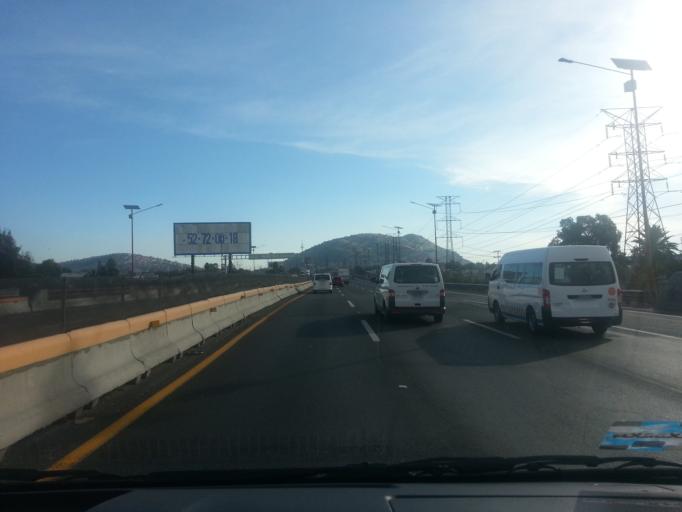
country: MX
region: Mexico
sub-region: Tlalnepantla de Baz
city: Puerto Escondido (Tepeolulco Puerto Escondido)
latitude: 19.5313
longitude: -99.0802
